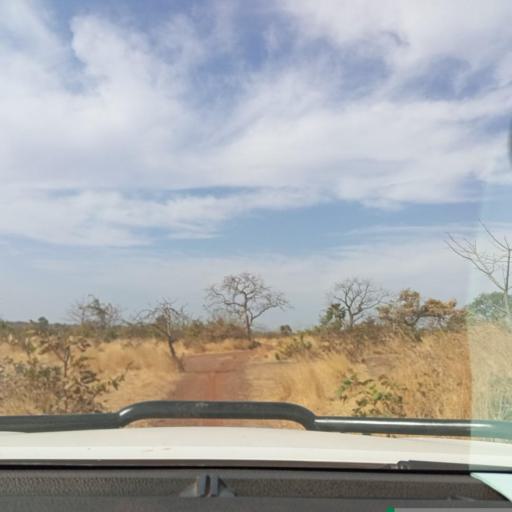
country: ML
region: Koulikoro
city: Kati
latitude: 12.7449
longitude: -8.2494
